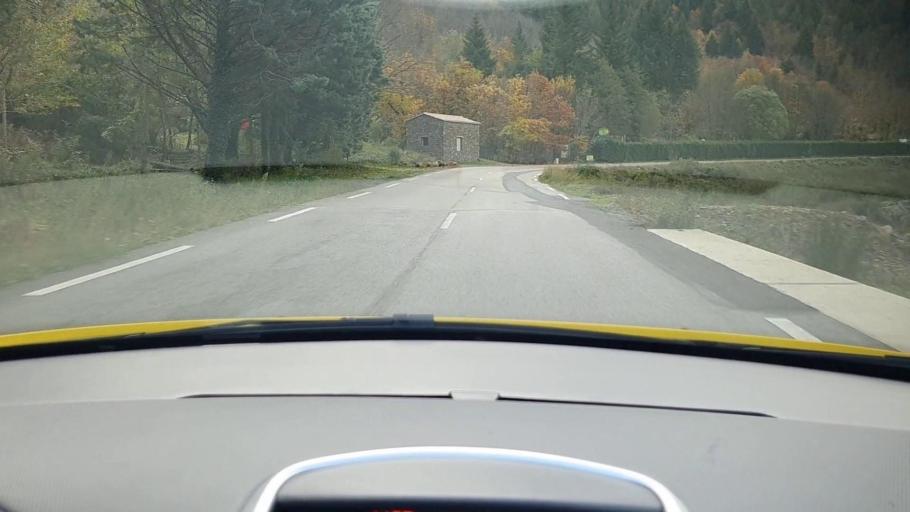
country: FR
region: Languedoc-Roussillon
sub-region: Departement du Gard
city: Lasalle
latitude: 44.1143
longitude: 3.7726
